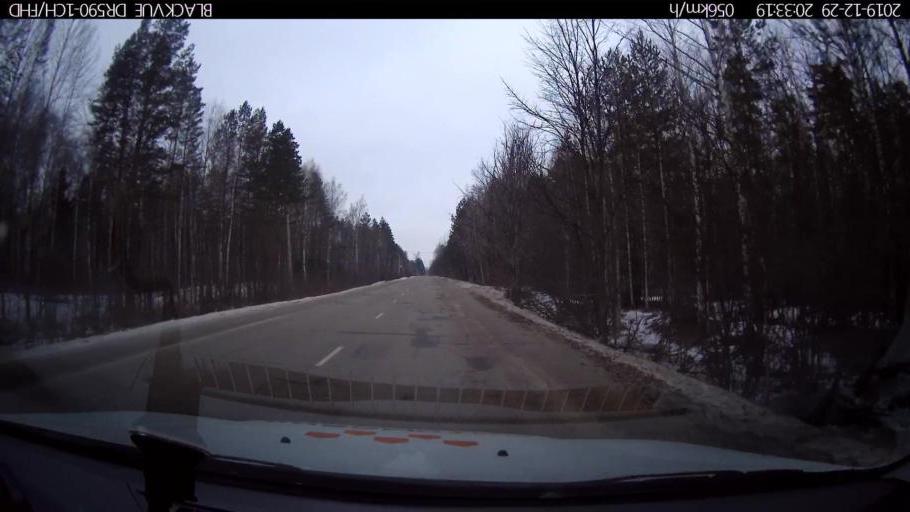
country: RU
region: Nizjnij Novgorod
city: Afonino
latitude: 56.1799
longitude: 44.0533
